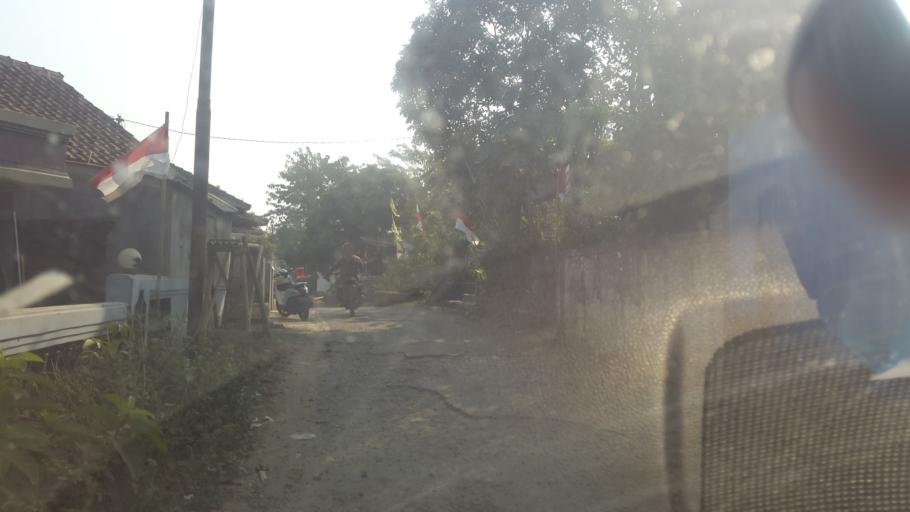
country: ID
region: West Java
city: Citanglar
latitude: -7.3205
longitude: 106.5832
